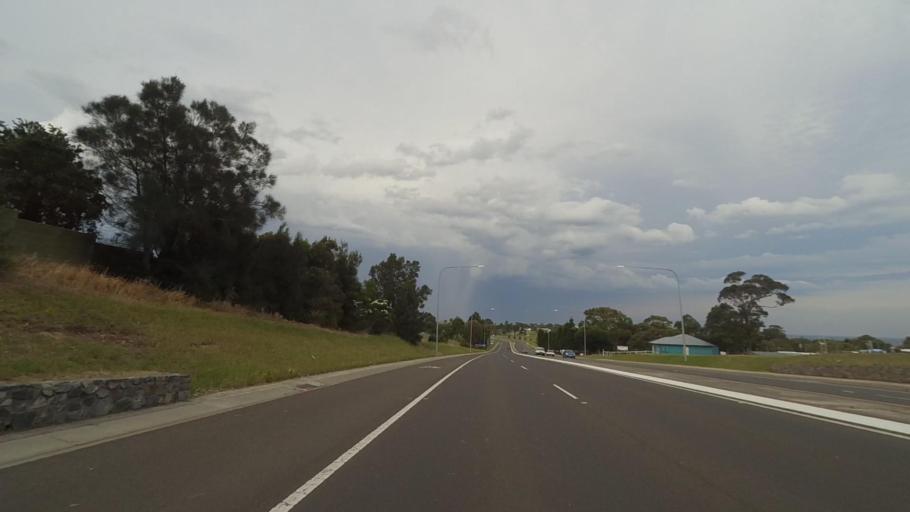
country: AU
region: New South Wales
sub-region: Shellharbour
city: Flinders
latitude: -34.5848
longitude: 150.8565
